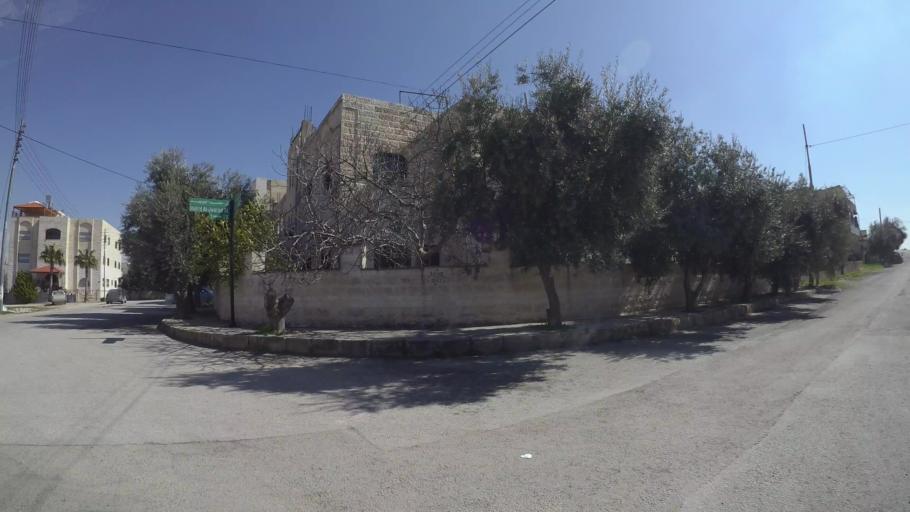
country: JO
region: Amman
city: Al Bunayyat ash Shamaliyah
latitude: 31.9063
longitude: 35.9048
